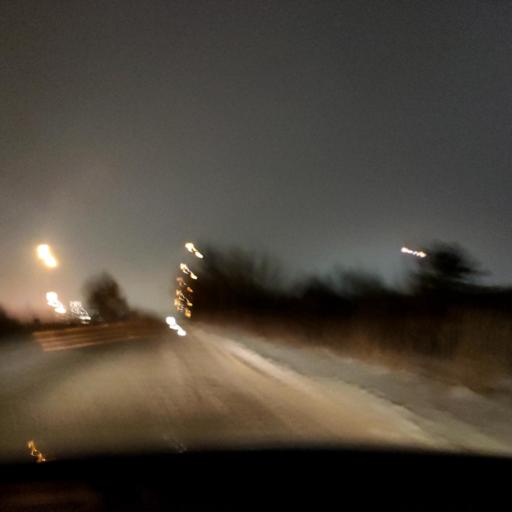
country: RU
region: Tatarstan
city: Staroye Arakchino
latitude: 55.8852
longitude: 48.9761
